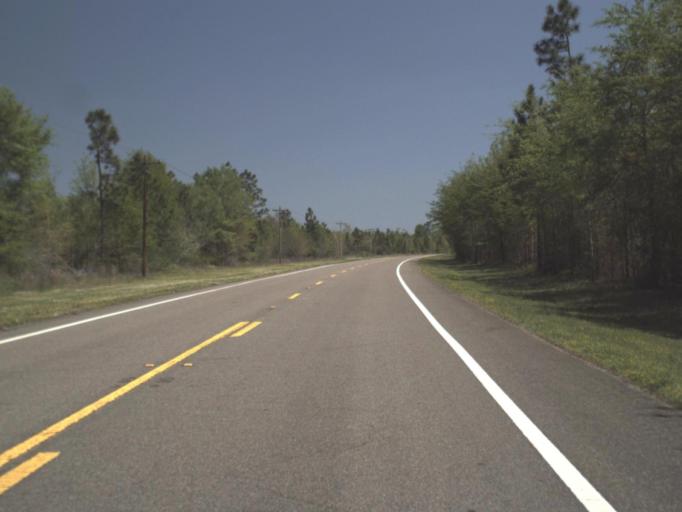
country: US
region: Alabama
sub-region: Escambia County
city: East Brewton
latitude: 30.9495
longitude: -87.0784
